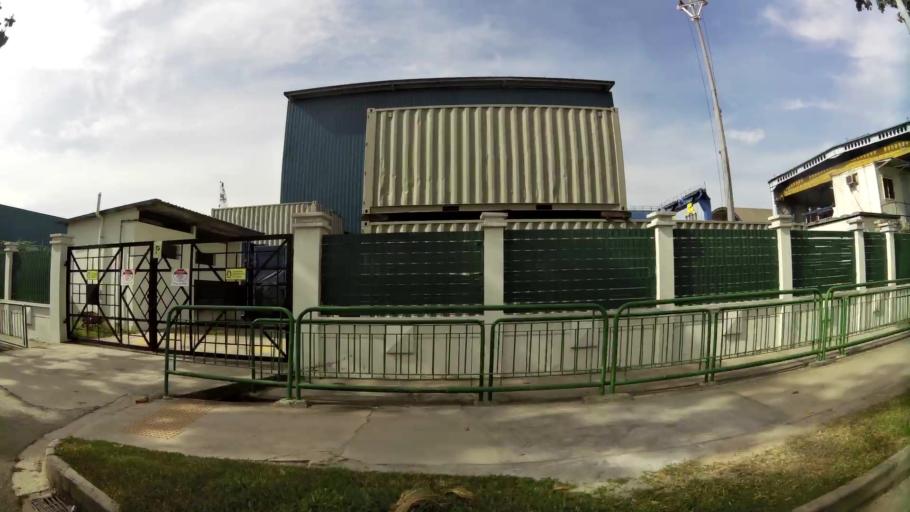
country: MY
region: Johor
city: Johor Bahru
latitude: 1.3173
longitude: 103.6512
